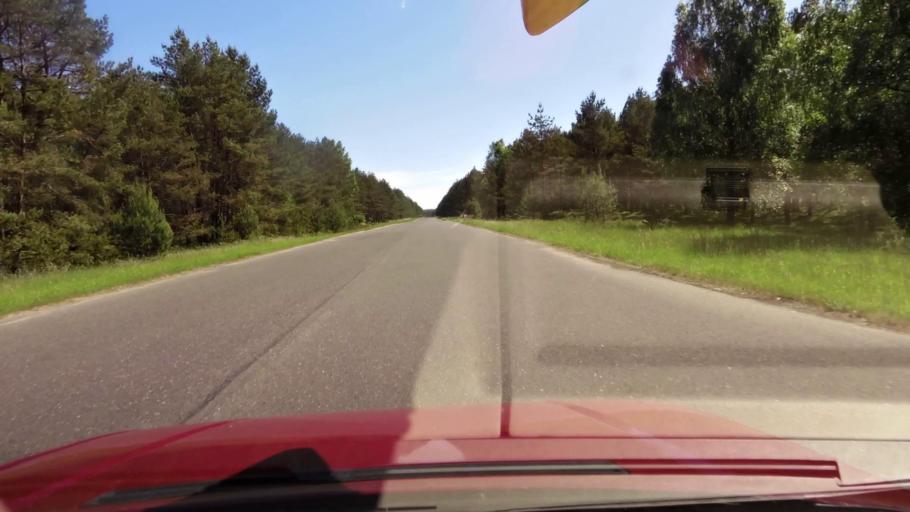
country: PL
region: West Pomeranian Voivodeship
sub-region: Powiat koszalinski
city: Bobolice
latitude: 54.0695
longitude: 16.5342
